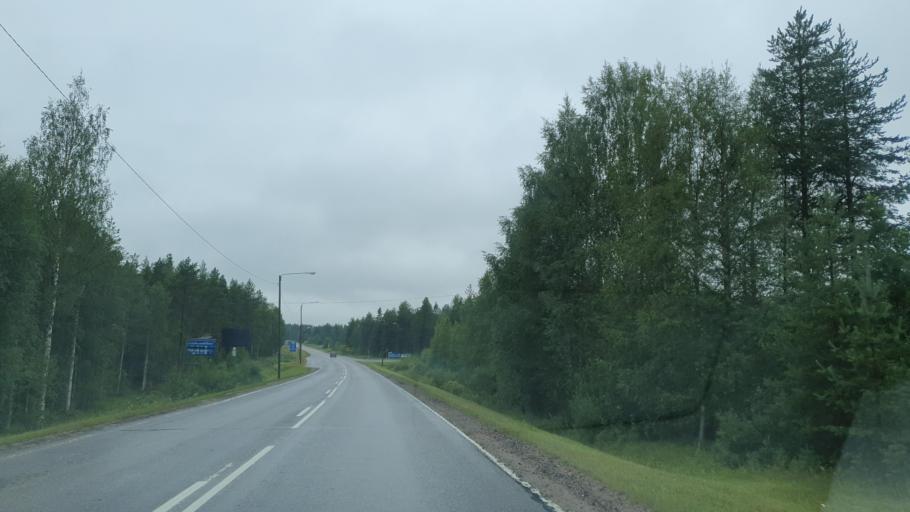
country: FI
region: Lapland
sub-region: Itae-Lappi
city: Kemijaervi
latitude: 66.7202
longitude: 27.3694
